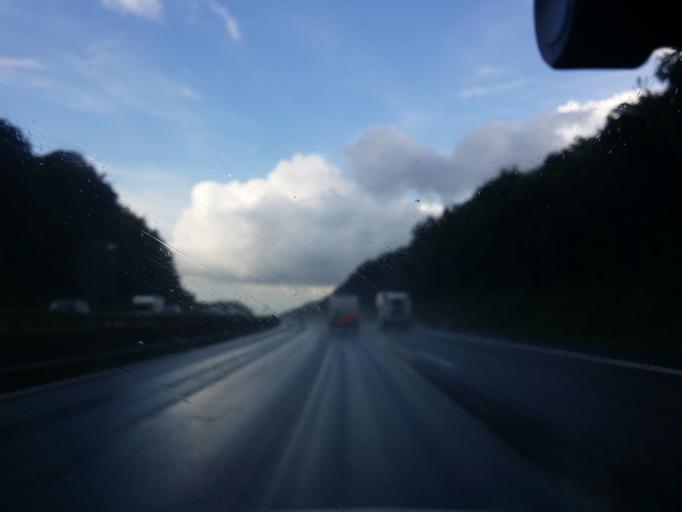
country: DE
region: Hesse
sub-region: Regierungsbezirk Kassel
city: Malsfeld
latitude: 51.0112
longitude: 9.4889
